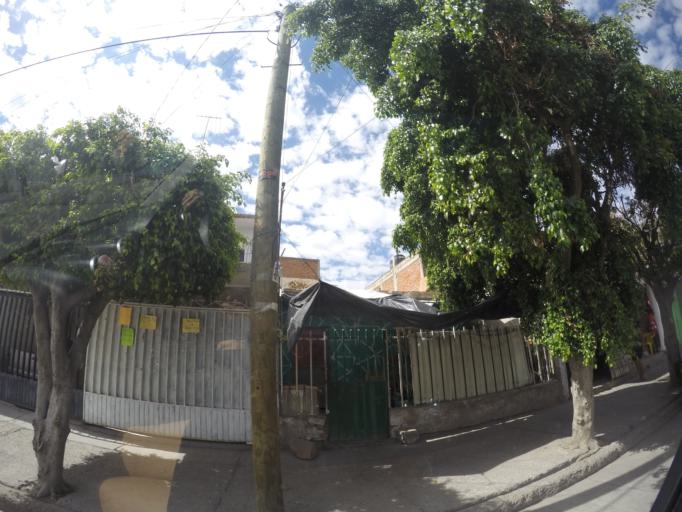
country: MX
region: Guanajuato
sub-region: Leon
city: San Jose de Duran (Los Troncoso)
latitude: 21.0947
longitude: -101.6803
